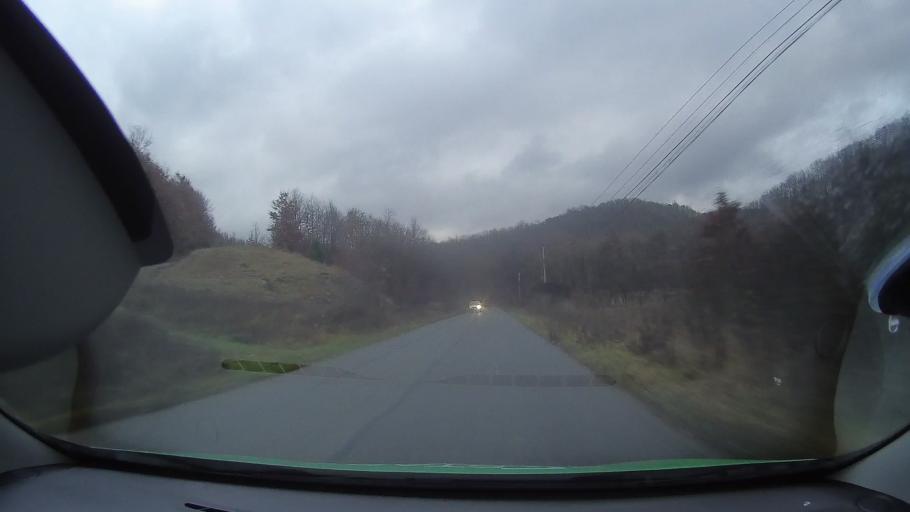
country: RO
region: Hunedoara
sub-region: Comuna Baia de Cris
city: Baia de Cris
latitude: 46.1938
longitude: 22.7174
